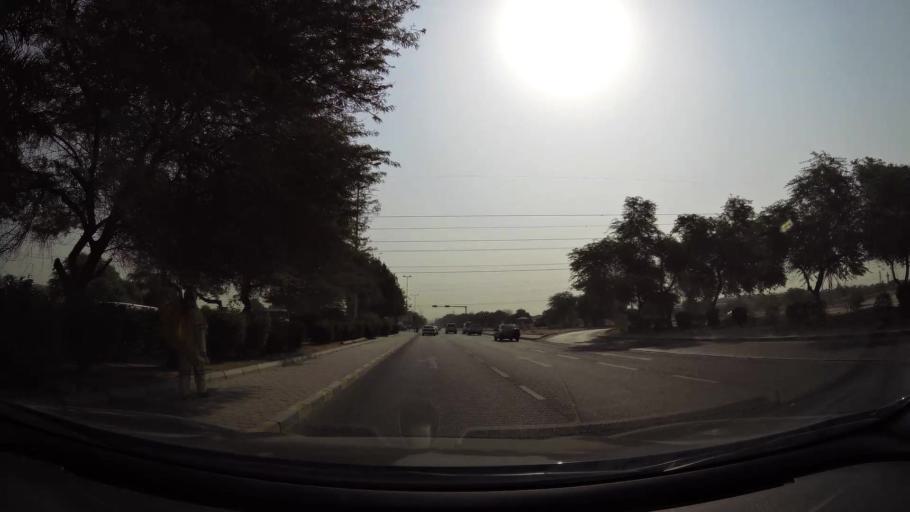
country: KW
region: Al Asimah
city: Ar Rabiyah
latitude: 29.2785
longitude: 47.8412
